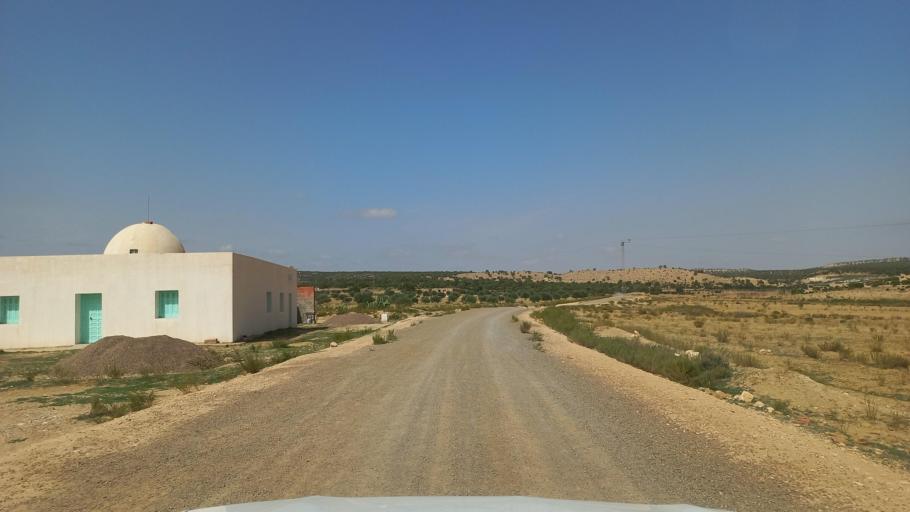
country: TN
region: Al Qasrayn
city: Sbiba
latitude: 35.3883
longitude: 8.9565
